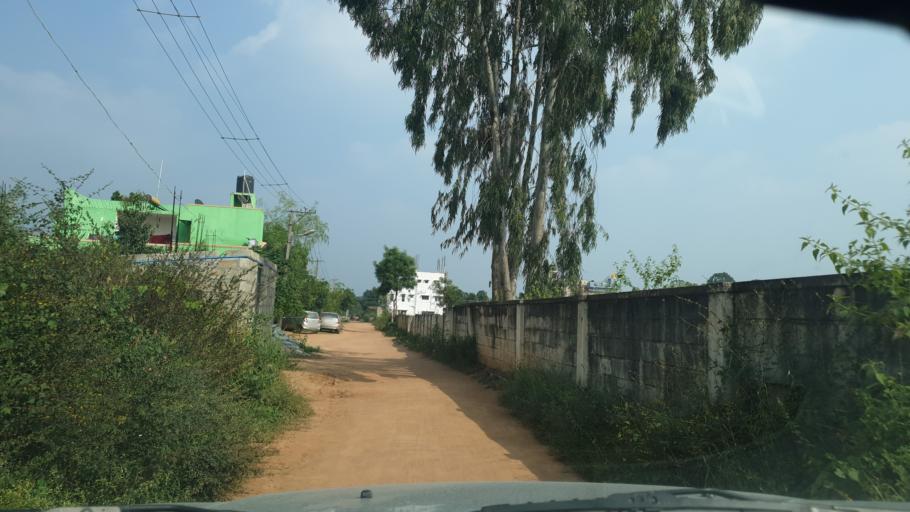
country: IN
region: Karnataka
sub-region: Bangalore Urban
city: Yelahanka
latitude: 13.0703
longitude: 77.6613
